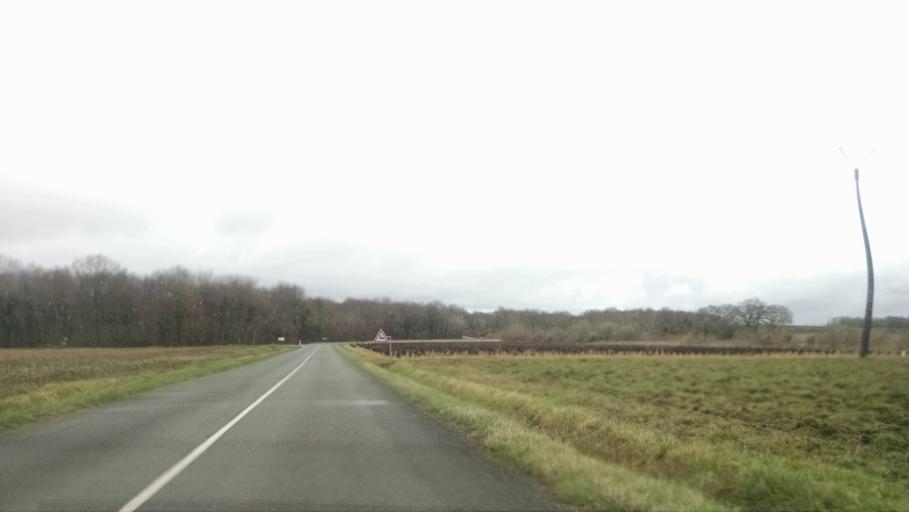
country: FR
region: Pays de la Loire
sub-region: Departement de la Loire-Atlantique
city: Maisdon-sur-Sevre
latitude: 47.1122
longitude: -1.3709
